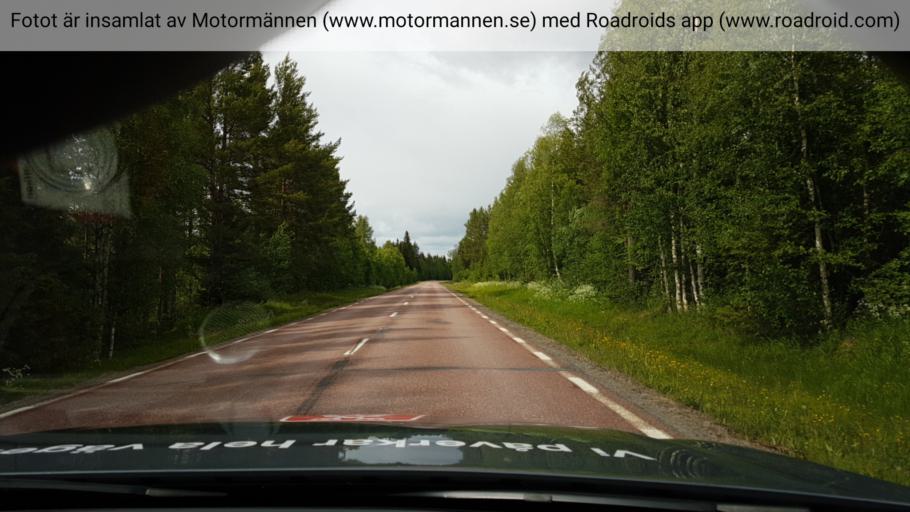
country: SE
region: Vaesterbotten
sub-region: Dorotea Kommun
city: Dorotea
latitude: 64.0899
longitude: 16.0857
